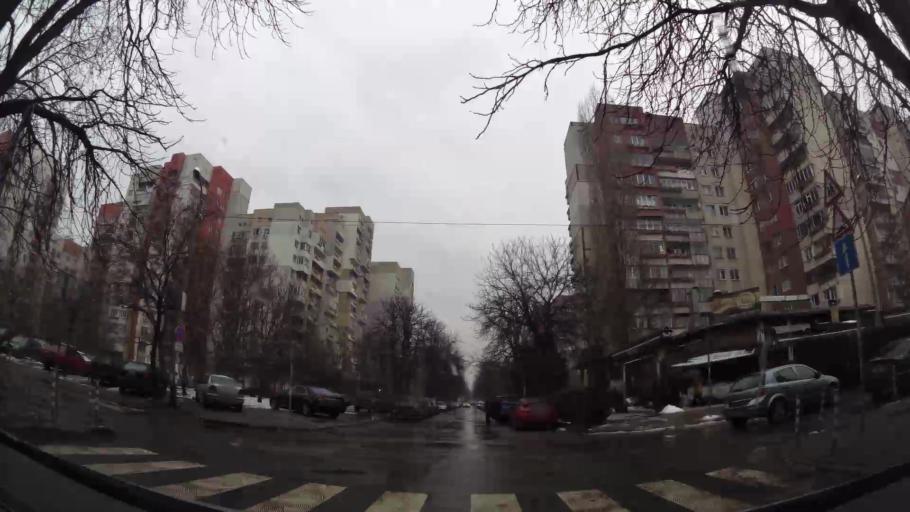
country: BG
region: Sofia-Capital
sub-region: Stolichna Obshtina
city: Sofia
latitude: 42.6761
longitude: 23.2943
